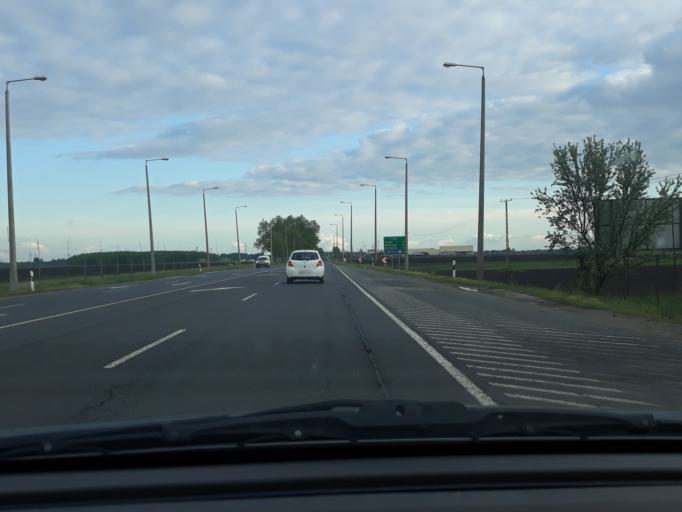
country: HU
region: Hajdu-Bihar
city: Mikepercs
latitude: 47.4849
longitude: 21.6332
